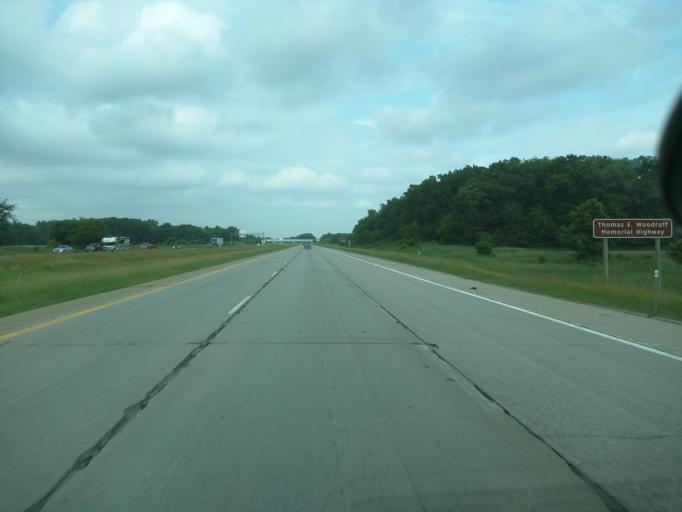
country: US
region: Michigan
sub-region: Clinton County
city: Bath
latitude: 42.8022
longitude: -84.4953
